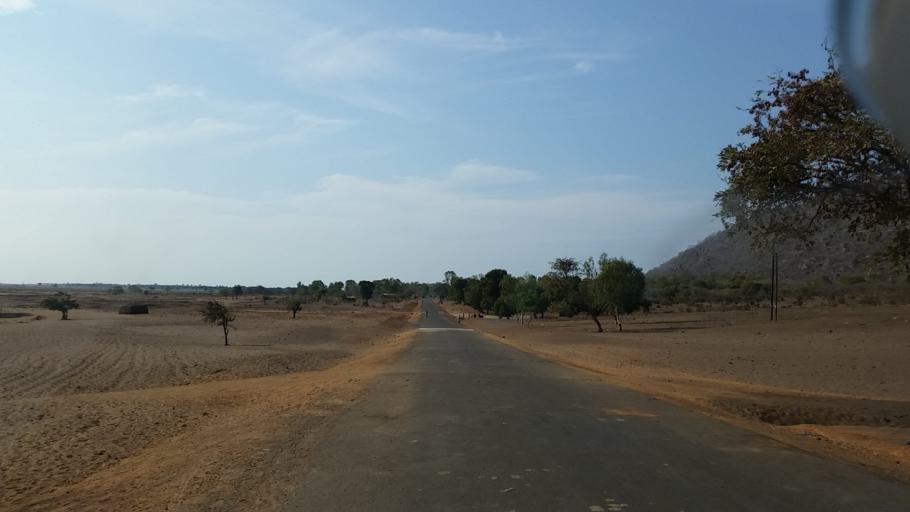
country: MW
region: Central Region
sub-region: Salima District
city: Salima
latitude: -13.6873
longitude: 34.5878
